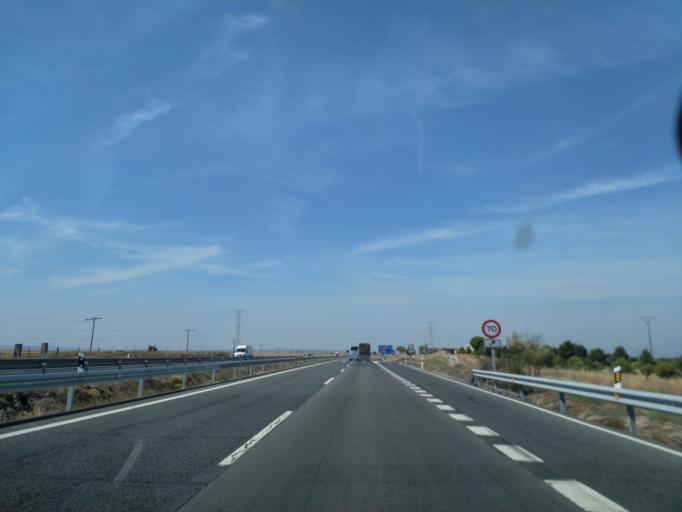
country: ES
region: Castille-La Mancha
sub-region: Province of Toledo
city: Caleruela
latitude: 39.8953
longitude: -5.3274
